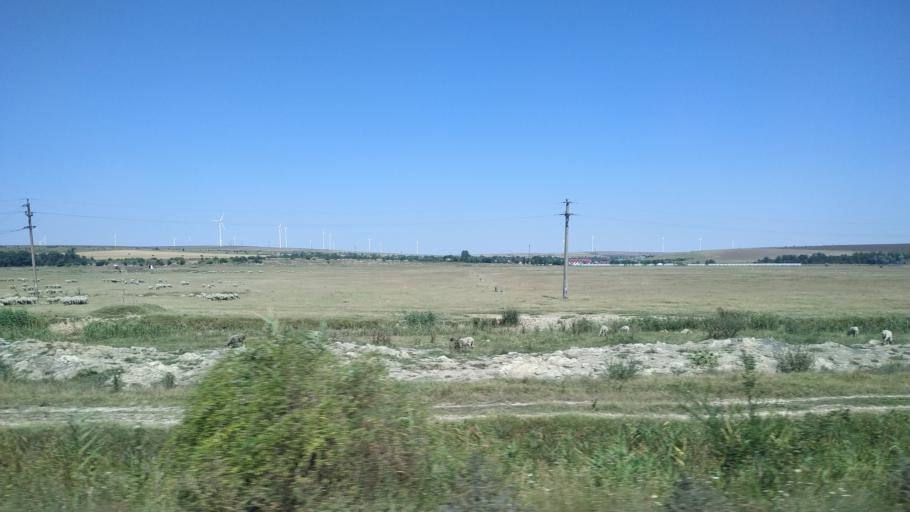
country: RO
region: Constanta
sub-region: Comuna Mircea Voda
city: Mircea Voda
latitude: 44.2639
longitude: 28.1692
